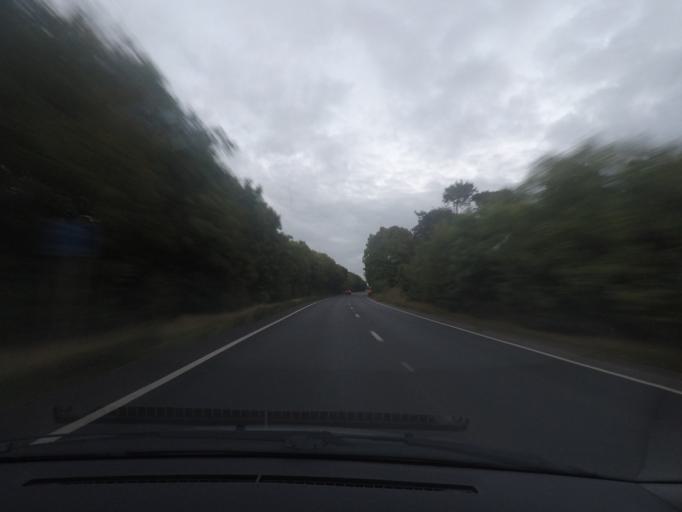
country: GB
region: England
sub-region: Northamptonshire
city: Stanwick
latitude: 52.3468
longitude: -0.5645
